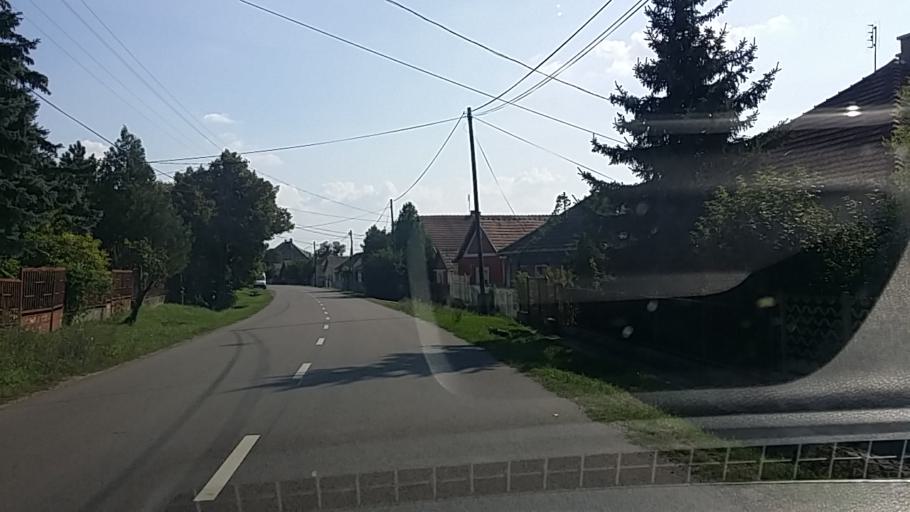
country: HU
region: Nograd
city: Palotas
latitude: 47.8256
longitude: 19.5873
